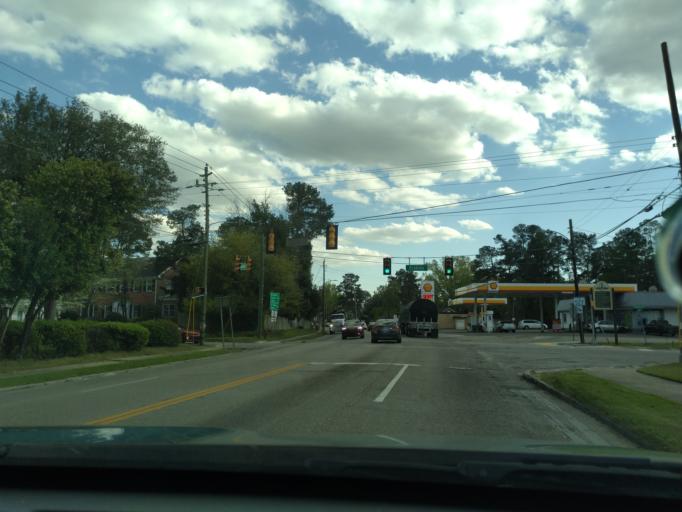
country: US
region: South Carolina
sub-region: Williamsburg County
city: Kingstree
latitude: 33.6719
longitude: -79.8360
